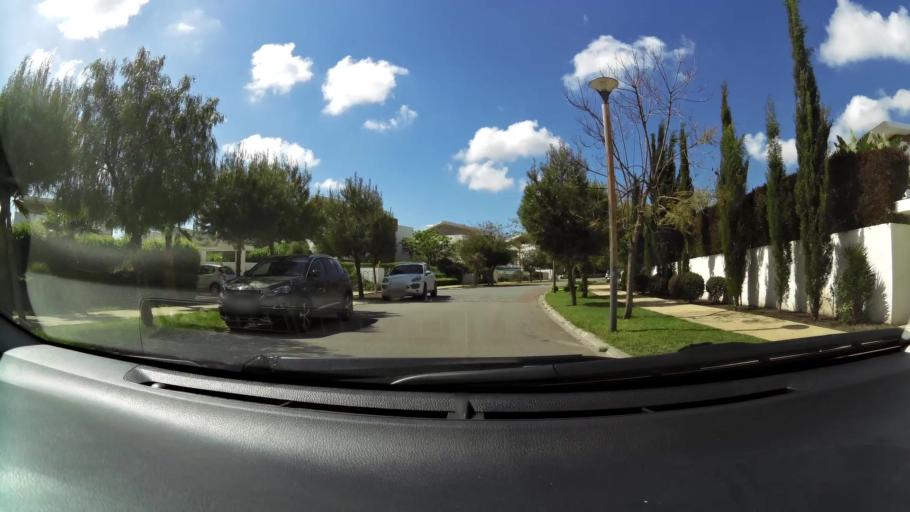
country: MA
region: Grand Casablanca
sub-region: Nouaceur
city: Bouskoura
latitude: 33.4924
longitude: -7.5965
